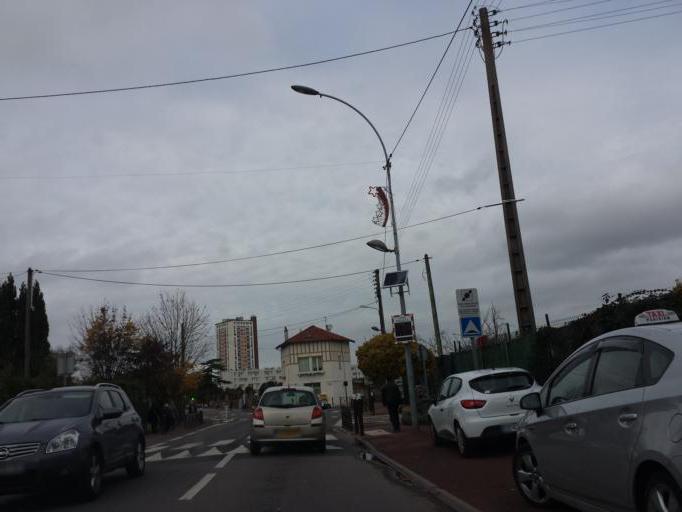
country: FR
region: Ile-de-France
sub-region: Departement du Val-d'Oise
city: Ermont
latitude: 48.9933
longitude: 2.2575
